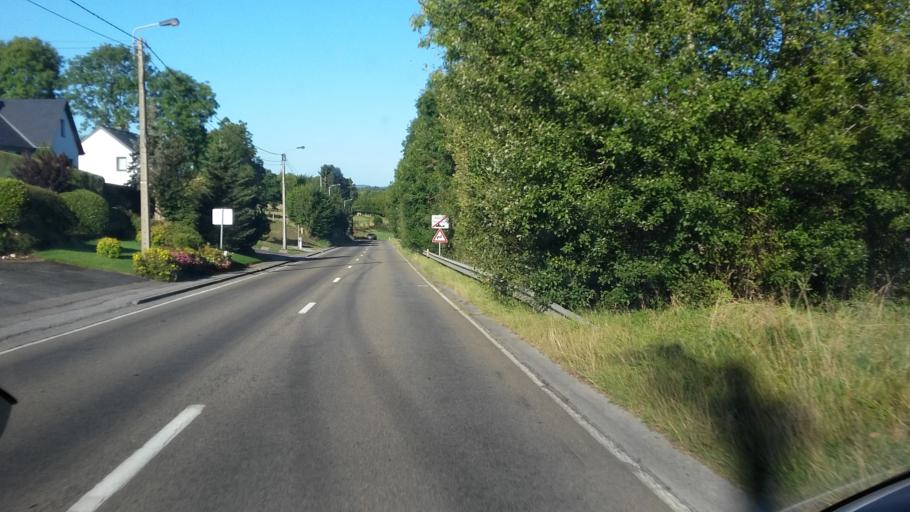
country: BE
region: Wallonia
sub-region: Province du Luxembourg
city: Neufchateau
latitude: 49.8380
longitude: 5.4531
